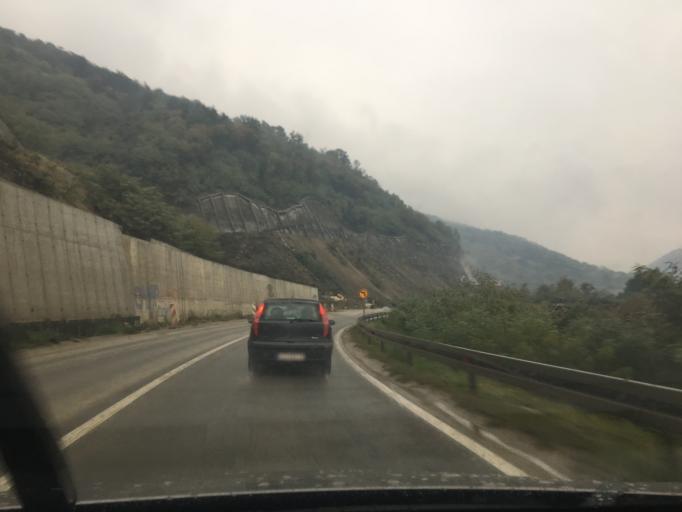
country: RS
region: Central Serbia
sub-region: Pcinjski Okrug
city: Vladicin Han
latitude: 42.7672
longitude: 22.0848
